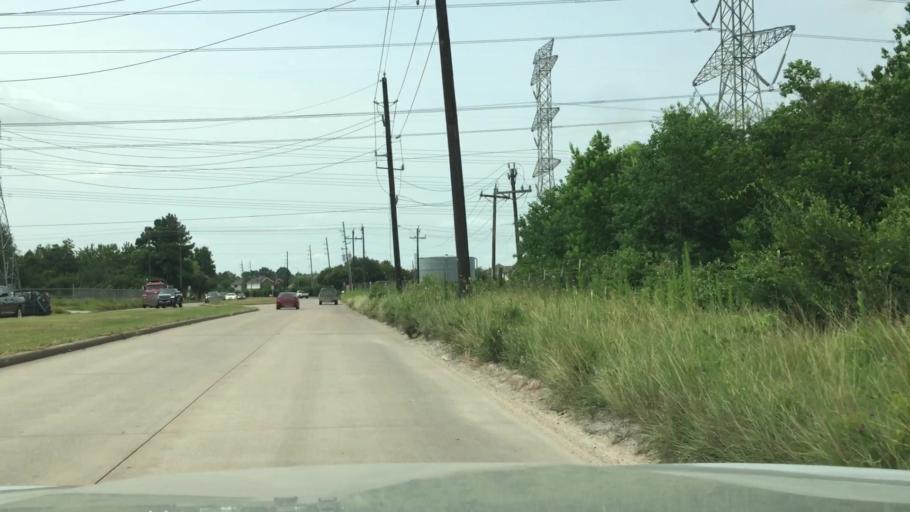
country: US
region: Texas
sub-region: Harris County
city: Jersey Village
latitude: 29.9390
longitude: -95.5469
